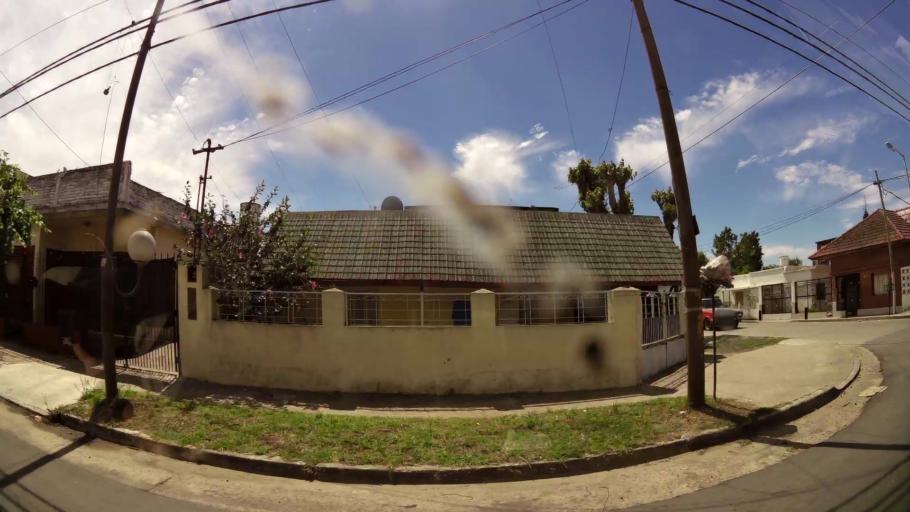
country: AR
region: Buenos Aires
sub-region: Partido de Quilmes
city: Quilmes
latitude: -34.7495
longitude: -58.2976
